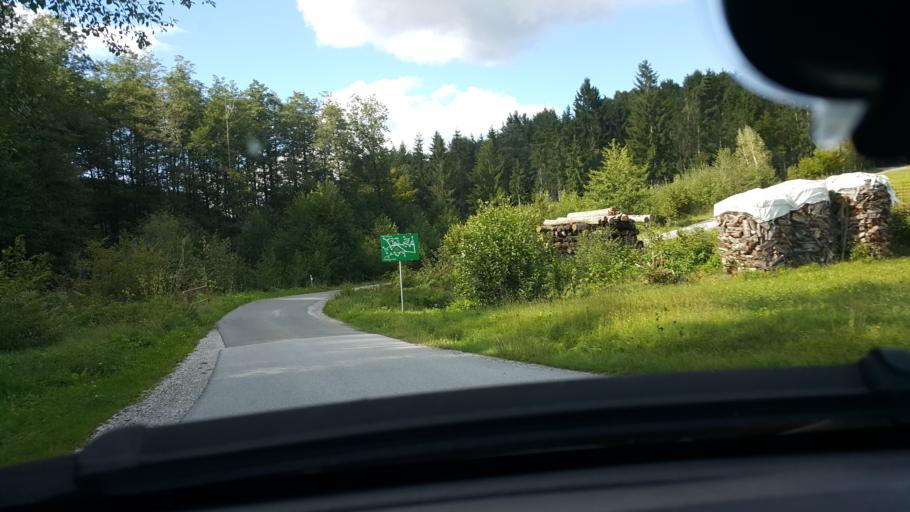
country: AT
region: Styria
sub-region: Politischer Bezirk Deutschlandsberg
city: Sankt Martin im Sulmtal
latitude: 46.7716
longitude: 15.2844
